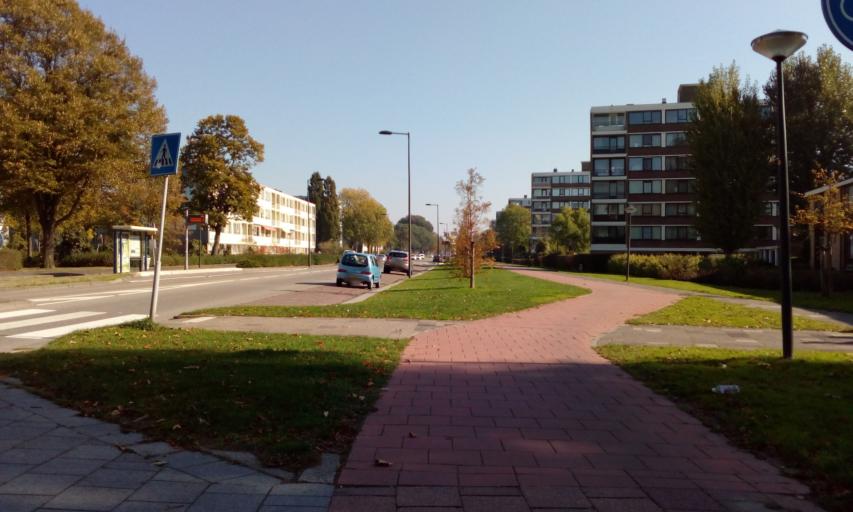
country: NL
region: South Holland
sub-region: Gemeente Vlaardingen
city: Vlaardingen
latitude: 51.9136
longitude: 4.3200
